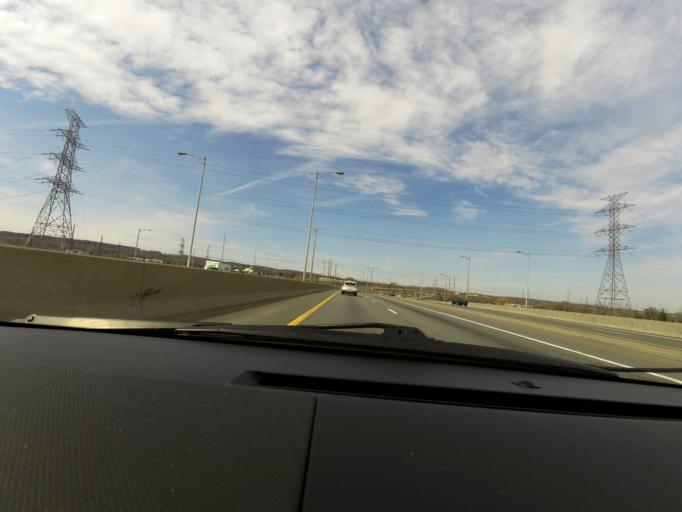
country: CA
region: Ontario
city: Burlington
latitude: 43.3298
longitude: -79.8268
